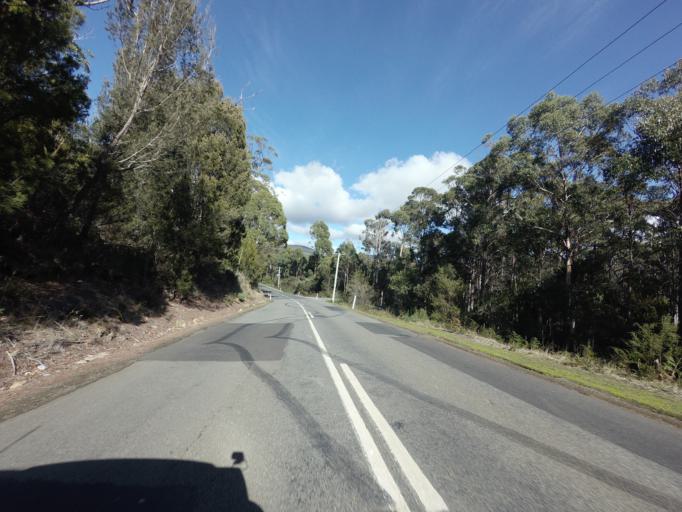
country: AU
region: Tasmania
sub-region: Clarence
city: Sandford
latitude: -43.0591
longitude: 147.8450
